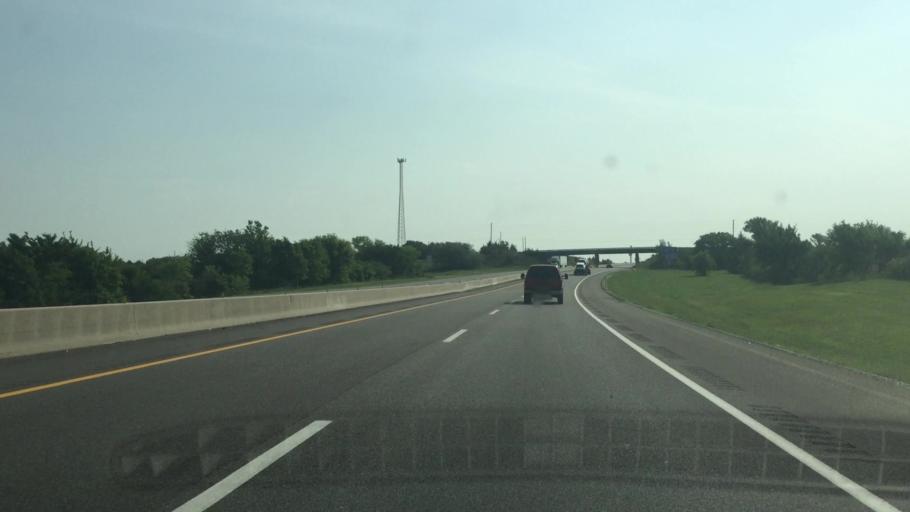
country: US
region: Kansas
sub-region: Butler County
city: Towanda
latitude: 37.7604
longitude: -97.0020
